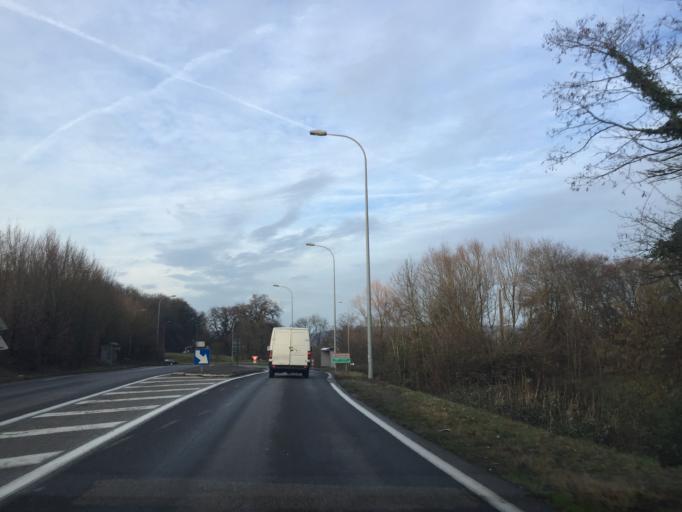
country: FR
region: Rhone-Alpes
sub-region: Departement de l'Isere
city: Vaulx-Milieu
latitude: 45.6106
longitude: 5.1716
